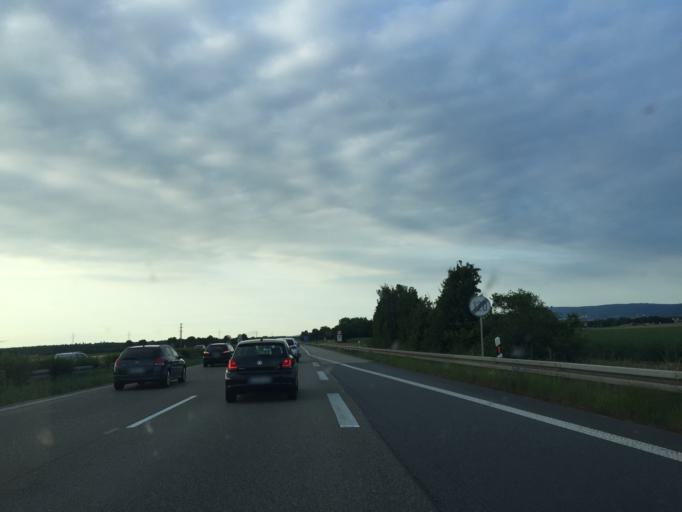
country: DE
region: Baden-Wuerttemberg
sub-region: Karlsruhe Region
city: Sankt Leon-Rot
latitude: 49.2885
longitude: 8.6237
